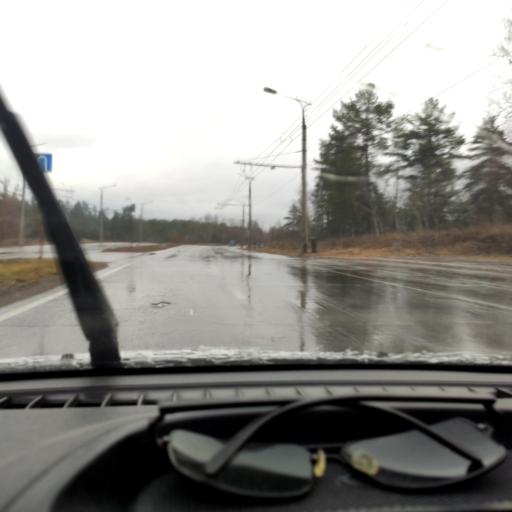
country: RU
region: Samara
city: Zhigulevsk
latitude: 53.5312
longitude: 49.5545
